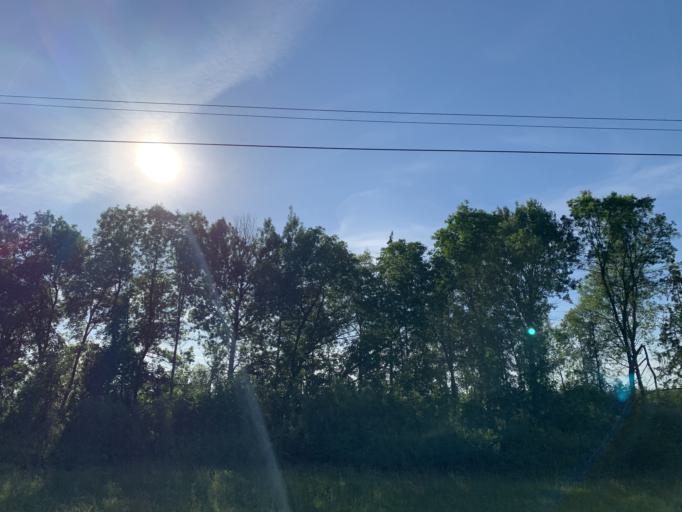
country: BY
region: Minsk
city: Haradzyeya
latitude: 53.3778
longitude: 26.5893
